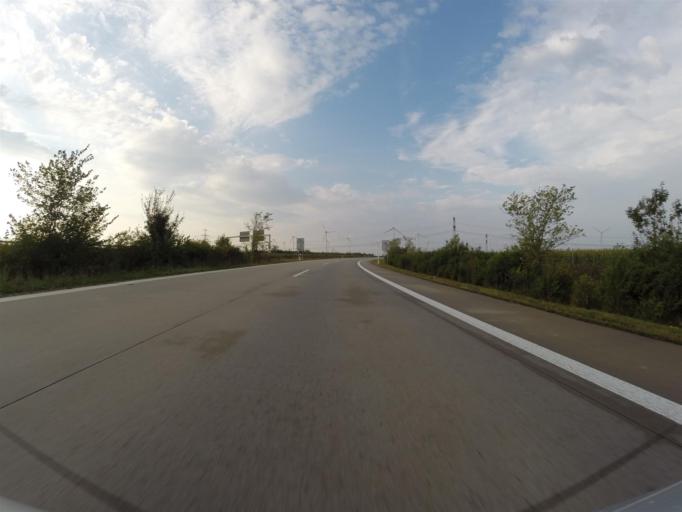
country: DE
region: Saxony-Anhalt
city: Bad Lauchstadt
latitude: 51.4062
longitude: 11.8595
